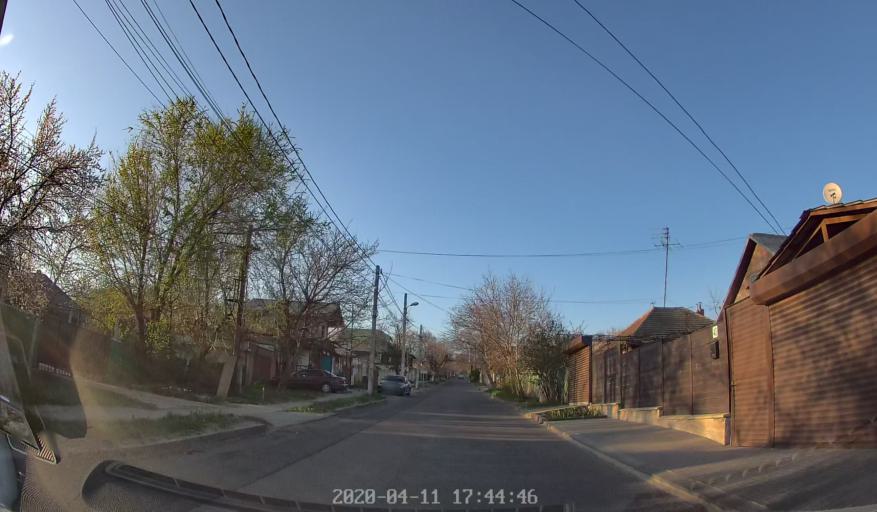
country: MD
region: Chisinau
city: Chisinau
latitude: 46.9799
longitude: 28.8235
